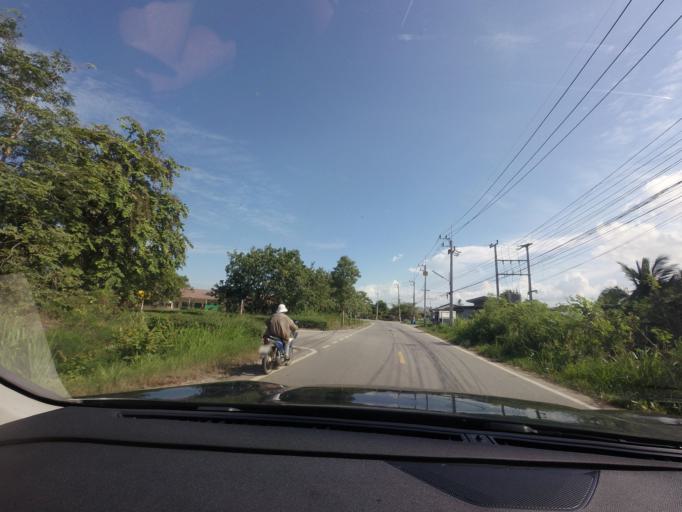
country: TH
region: Prachuap Khiri Khan
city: Pran Buri
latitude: 12.4346
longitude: 99.9443
